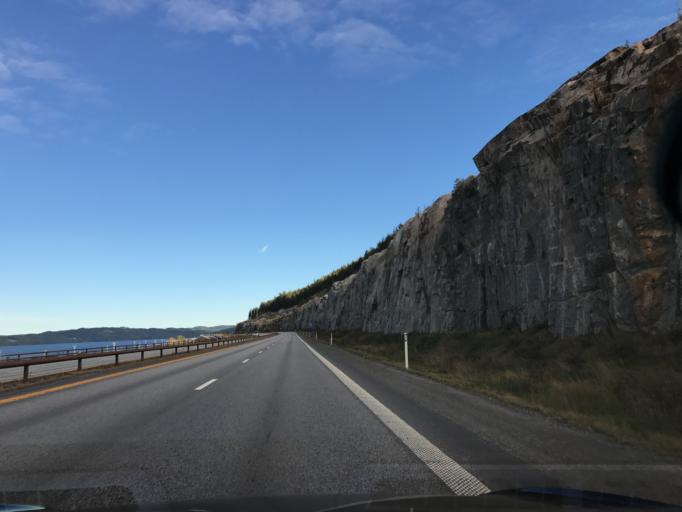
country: NO
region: Hedmark
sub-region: Stange
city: Stange
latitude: 60.5415
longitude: 11.2464
